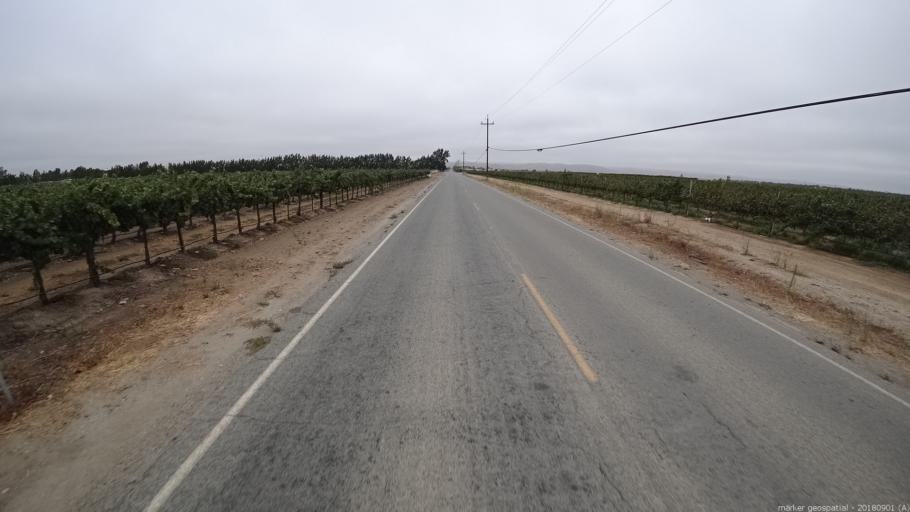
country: US
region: California
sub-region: Monterey County
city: Greenfield
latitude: 36.3070
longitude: -121.2602
